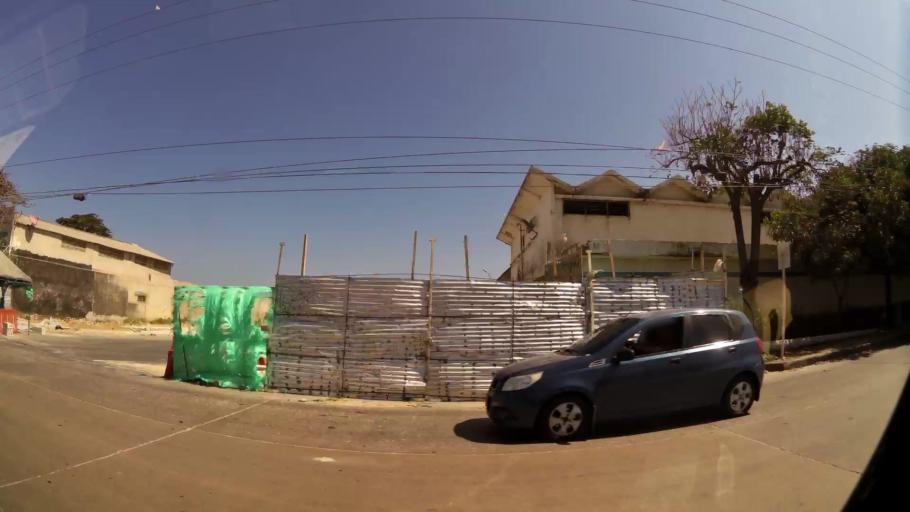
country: CO
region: Atlantico
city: Barranquilla
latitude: 11.0197
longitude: -74.7980
